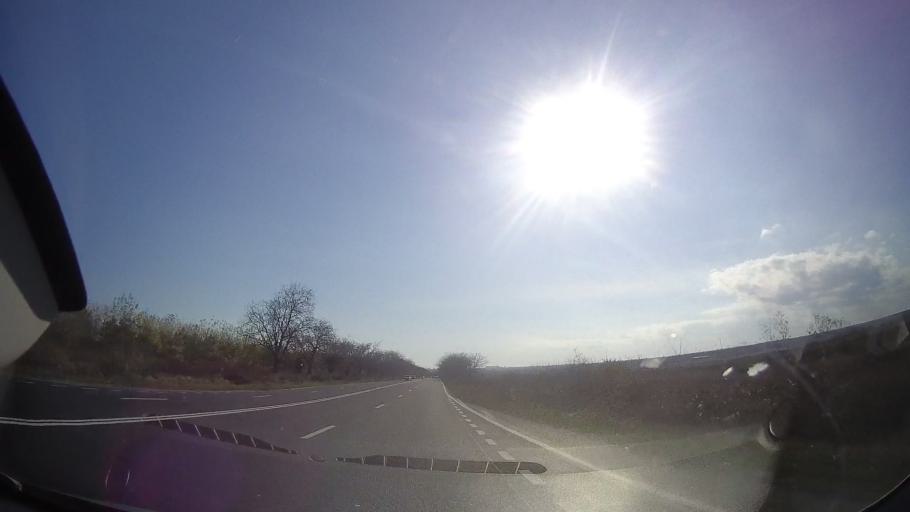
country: RO
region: Constanta
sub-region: Municipiul Mangalia
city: Mangalia
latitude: 43.8549
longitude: 28.5760
